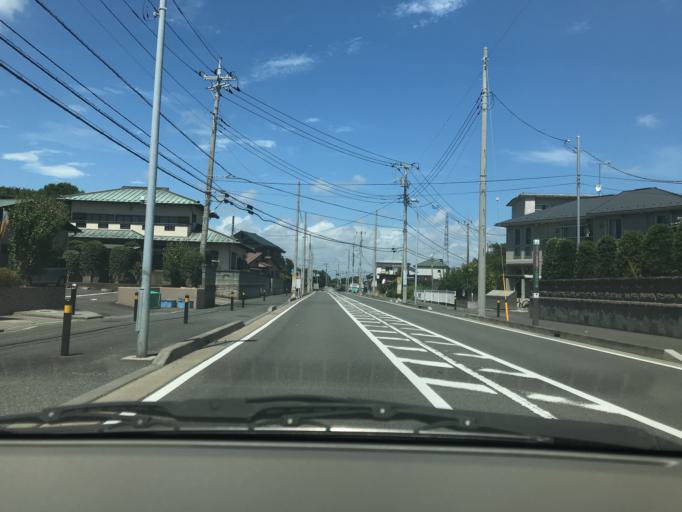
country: JP
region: Kanagawa
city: Fujisawa
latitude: 35.3646
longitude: 139.4611
